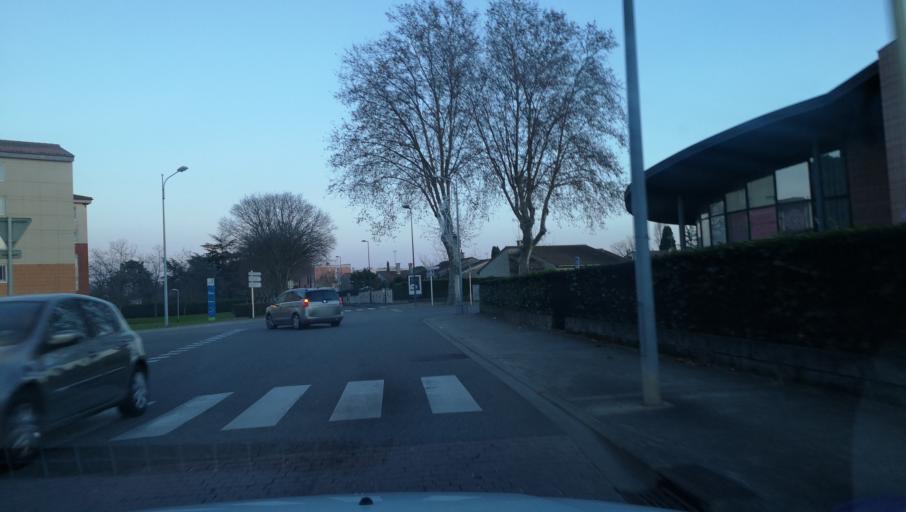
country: FR
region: Midi-Pyrenees
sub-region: Departement de la Haute-Garonne
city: Blagnac
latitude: 43.6382
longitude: 1.3804
